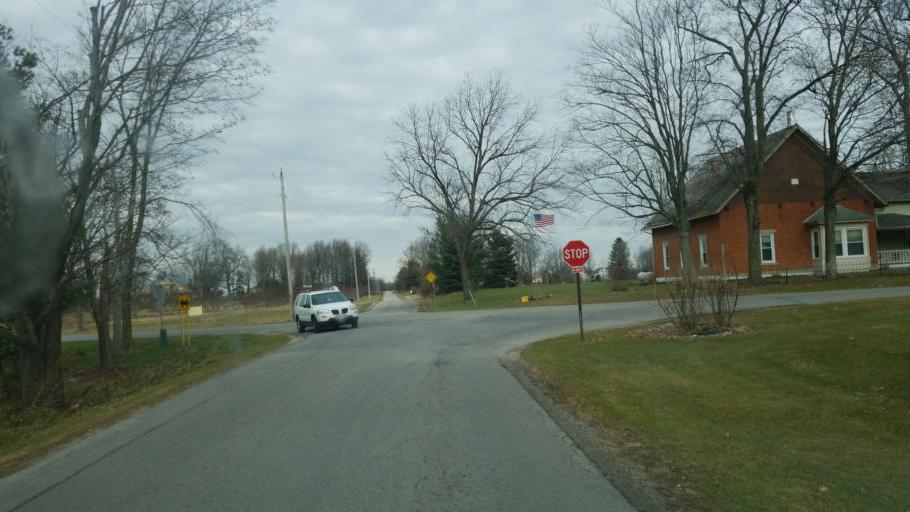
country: US
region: Ohio
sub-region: Crawford County
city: Galion
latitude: 40.7699
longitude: -82.7829
